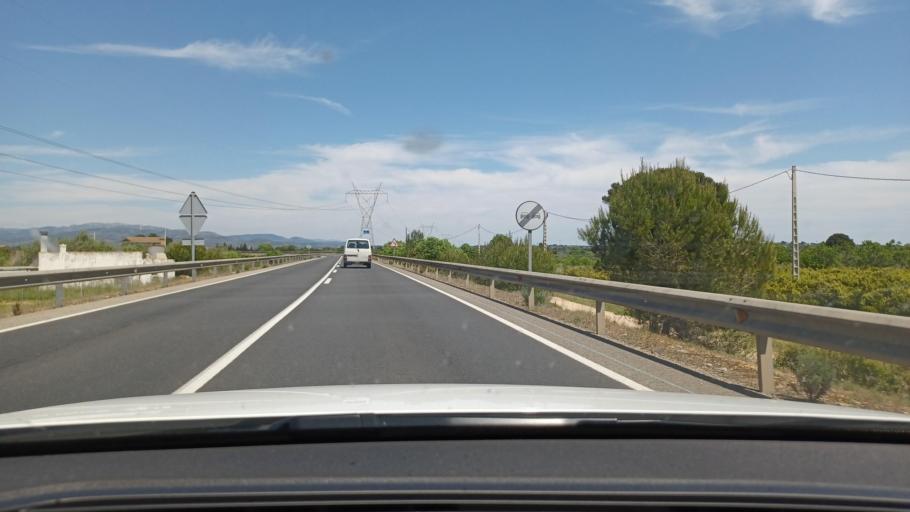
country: ES
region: Catalonia
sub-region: Provincia de Tarragona
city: Santa Barbara
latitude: 40.7076
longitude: 0.5043
